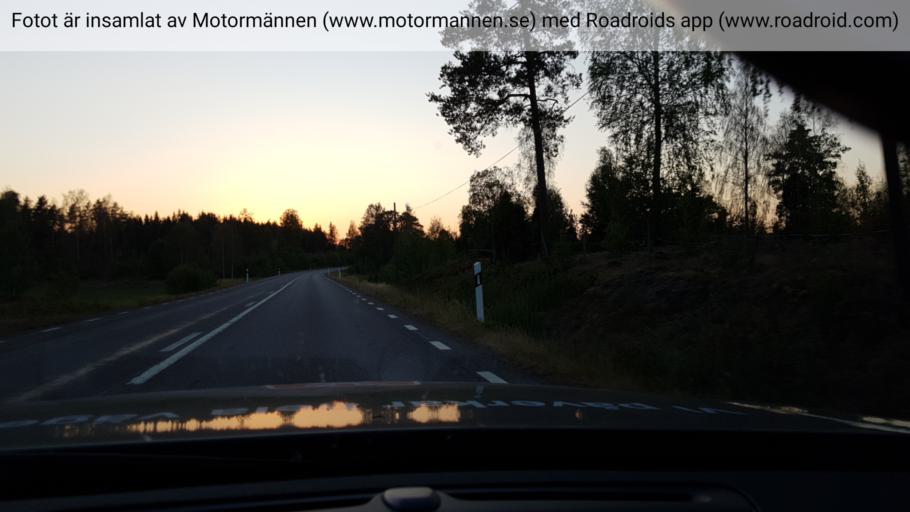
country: SE
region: Uppsala
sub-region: Heby Kommun
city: OEstervala
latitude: 60.0782
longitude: 17.1972
